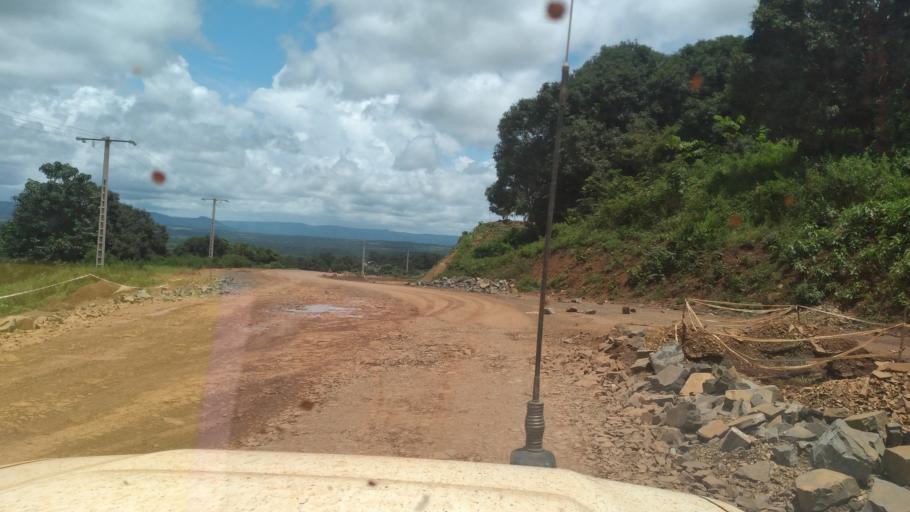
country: GN
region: Kindia
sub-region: Kindia
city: Kindia
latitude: 10.1778
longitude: -12.4775
